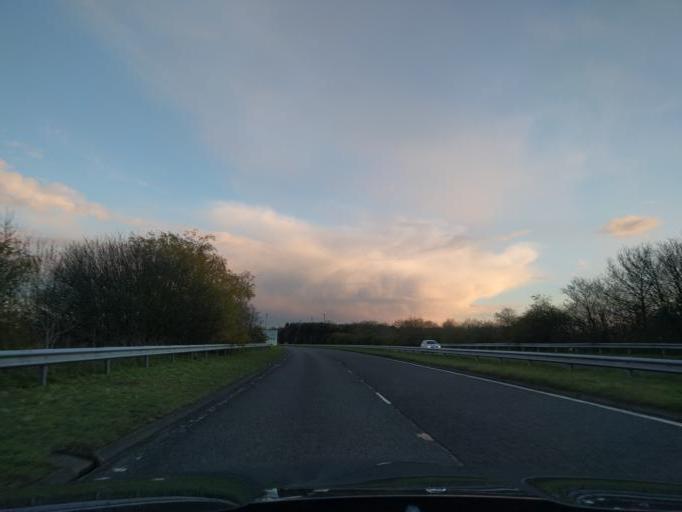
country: GB
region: England
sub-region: Northumberland
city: Cramlington
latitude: 55.0431
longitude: -1.5916
